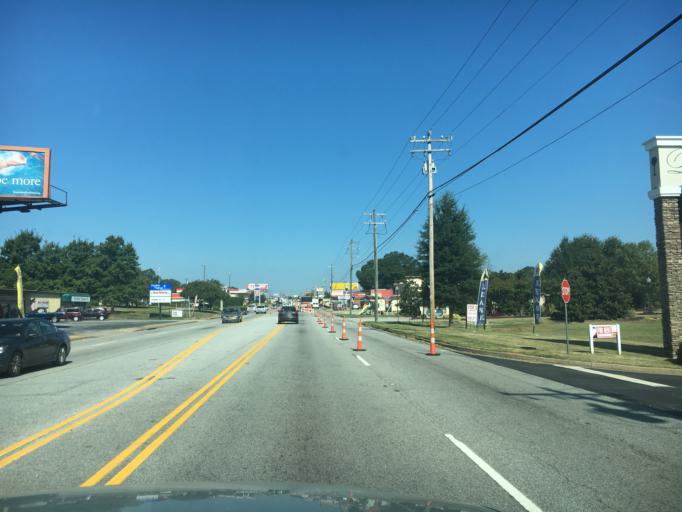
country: US
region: South Carolina
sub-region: Spartanburg County
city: Boiling Springs
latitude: 35.0336
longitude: -81.9703
